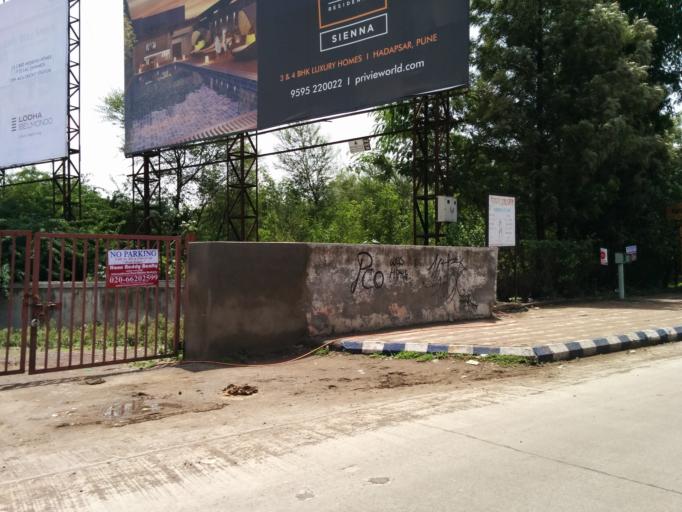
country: IN
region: Maharashtra
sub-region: Pune Division
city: Pune
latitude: 18.5348
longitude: 73.9129
